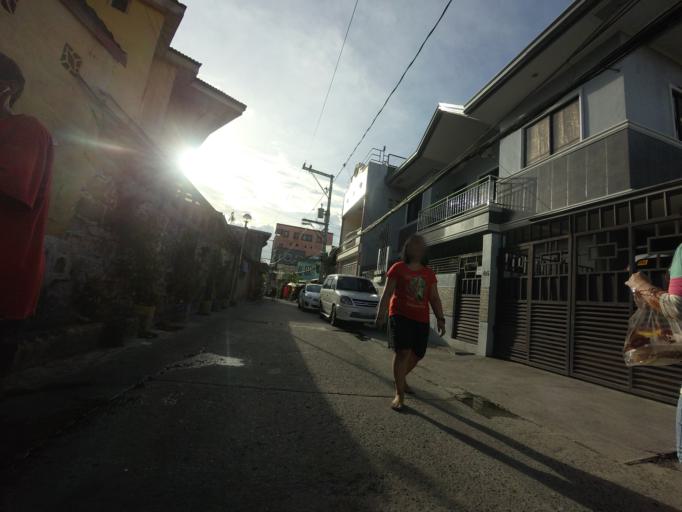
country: PH
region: Metro Manila
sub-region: Mandaluyong
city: Mandaluyong City
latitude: 14.5697
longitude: 121.0392
